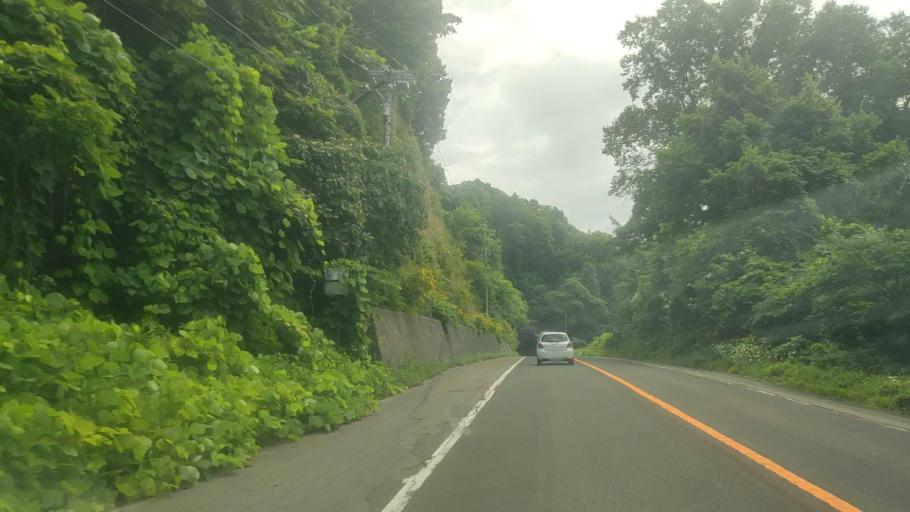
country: JP
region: Hokkaido
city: Niseko Town
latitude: 42.5906
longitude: 140.6759
